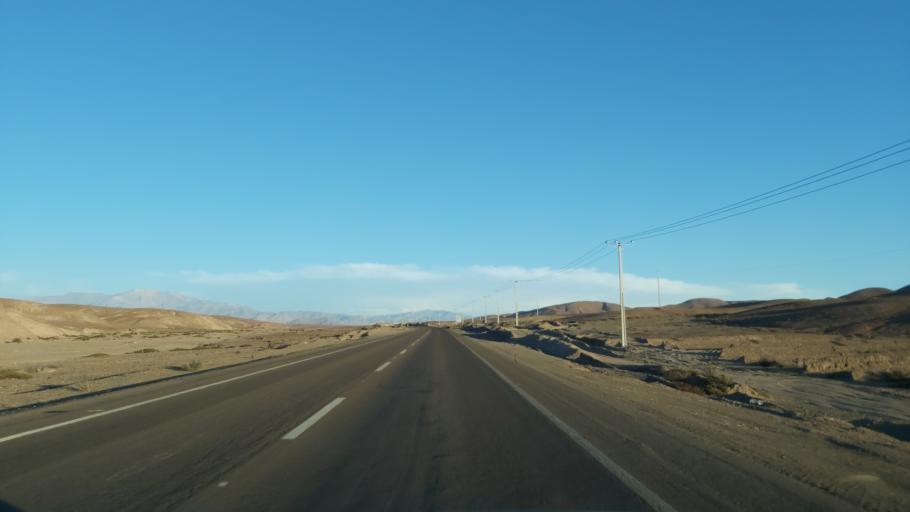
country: CL
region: Atacama
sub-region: Provincia de Chanaral
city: Diego de Almagro
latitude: -26.4246
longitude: -70.0195
